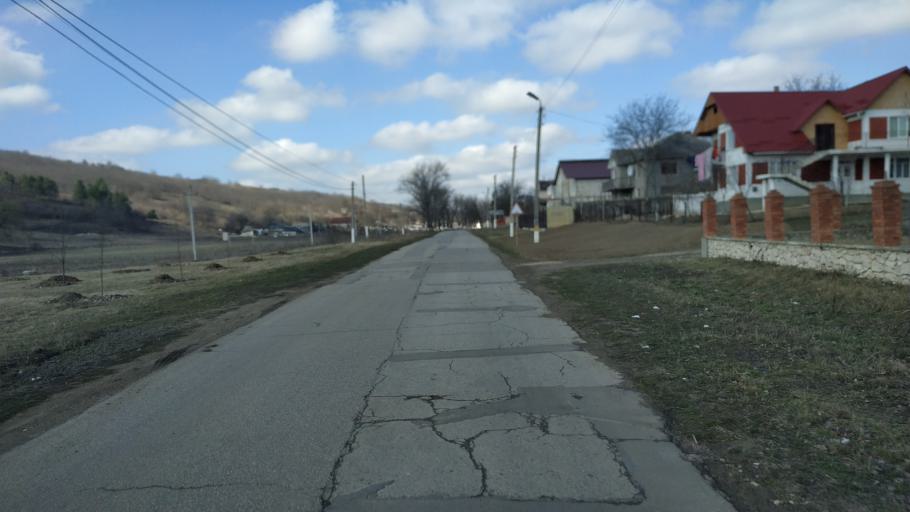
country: MD
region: Hincesti
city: Hincesti
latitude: 46.8720
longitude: 28.6345
